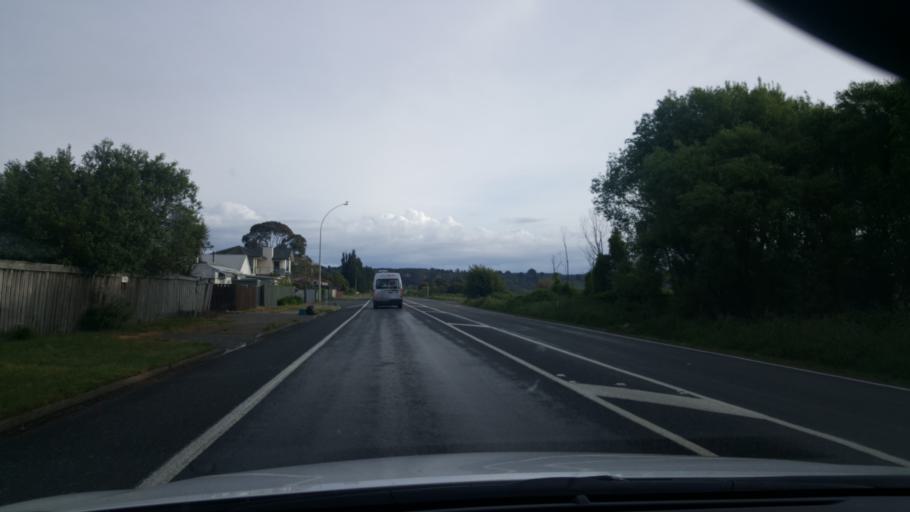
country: NZ
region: Waikato
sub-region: Taupo District
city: Taupo
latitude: -38.7814
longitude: 176.0769
